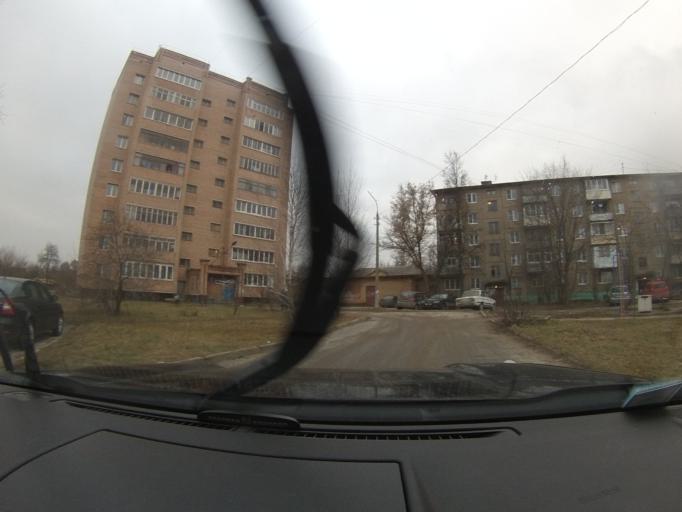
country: RU
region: Moskovskaya
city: Peski
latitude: 55.2475
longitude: 38.7667
